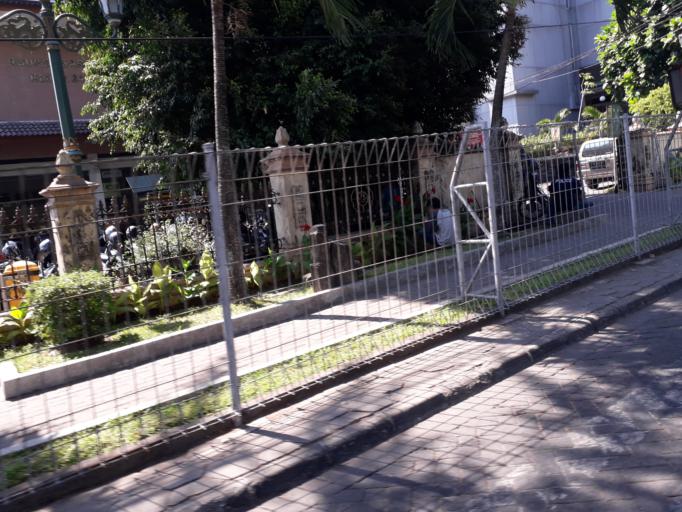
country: ID
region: Daerah Istimewa Yogyakarta
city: Yogyakarta
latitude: -7.7688
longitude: 110.3739
